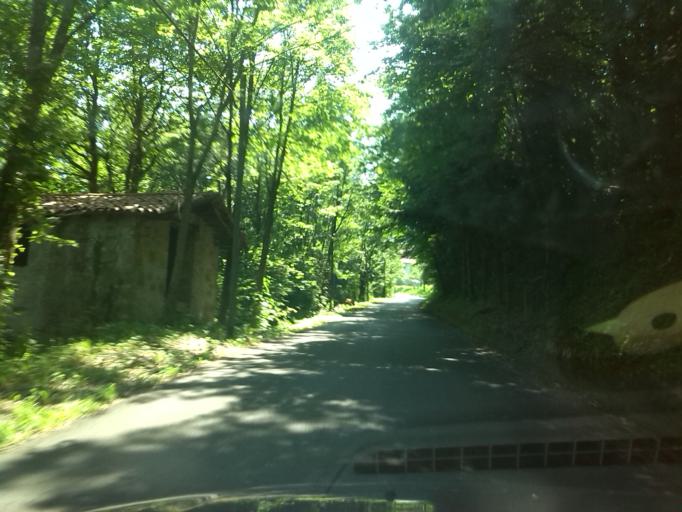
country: IT
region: Friuli Venezia Giulia
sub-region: Provincia di Udine
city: Stregna
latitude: 46.1270
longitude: 13.5914
